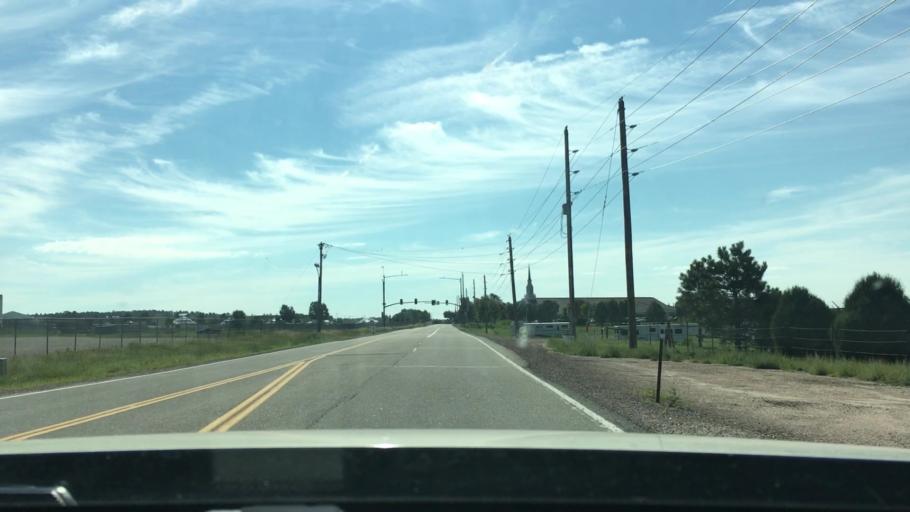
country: US
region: Colorado
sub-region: Douglas County
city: The Pinery
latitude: 39.4338
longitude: -104.7560
